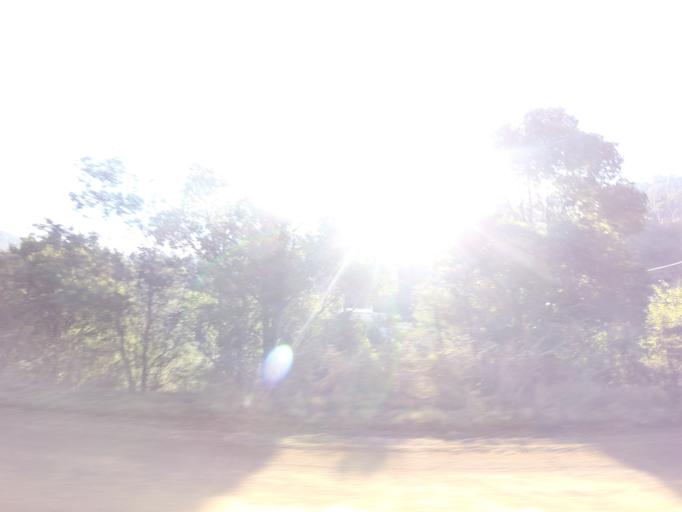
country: AU
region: Tasmania
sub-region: Sorell
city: Sorell
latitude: -42.4887
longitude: 147.4337
